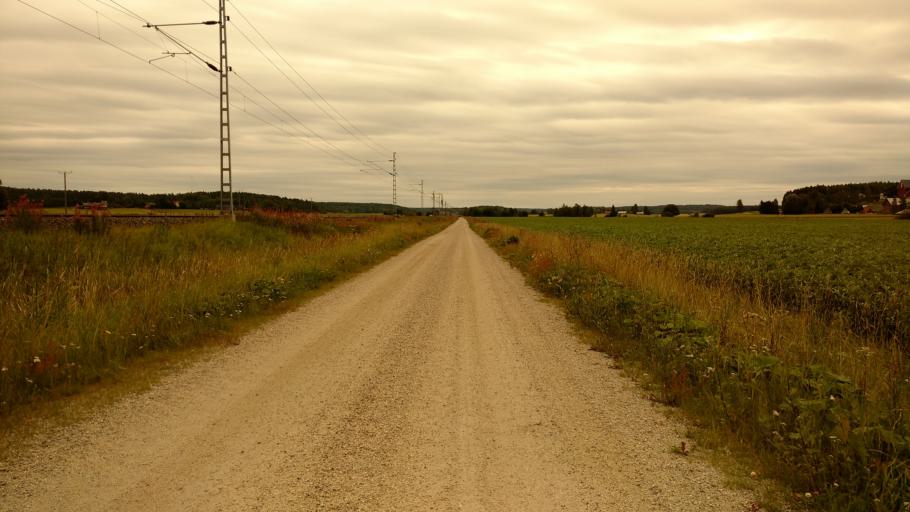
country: FI
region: Varsinais-Suomi
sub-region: Turku
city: Paimio
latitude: 60.4219
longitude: 22.8226
